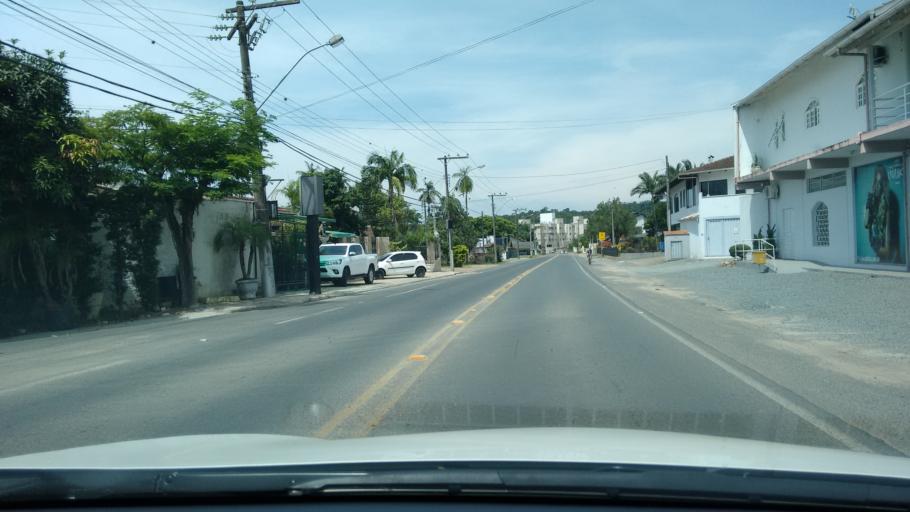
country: BR
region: Santa Catarina
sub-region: Timbo
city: Timbo
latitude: -26.8267
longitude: -49.2882
